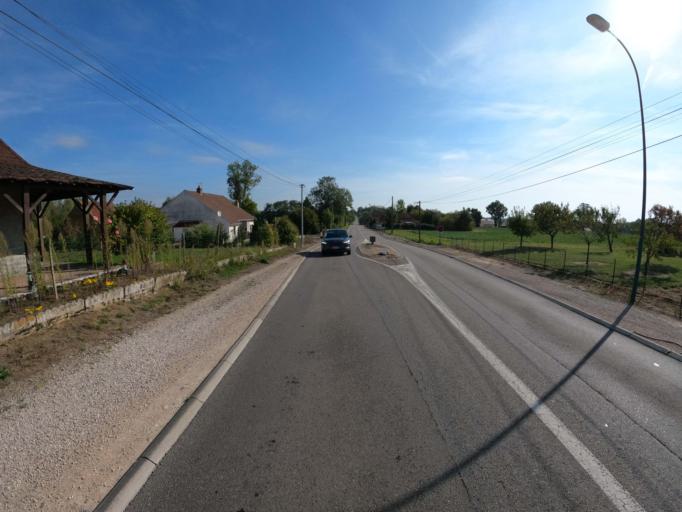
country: FR
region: Bourgogne
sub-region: Departement de Saone-et-Loire
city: Saint-Martin-en-Bresse
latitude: 46.7415
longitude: 5.0978
